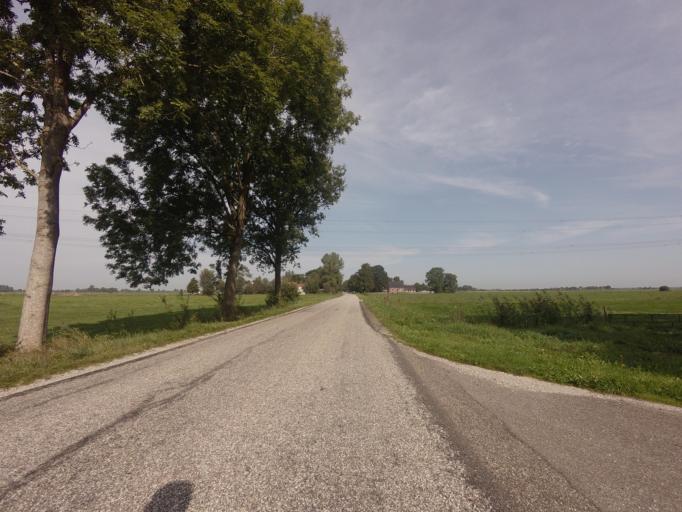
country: NL
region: Groningen
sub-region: Gemeente Leek
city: Leek
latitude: 53.1946
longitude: 6.3538
